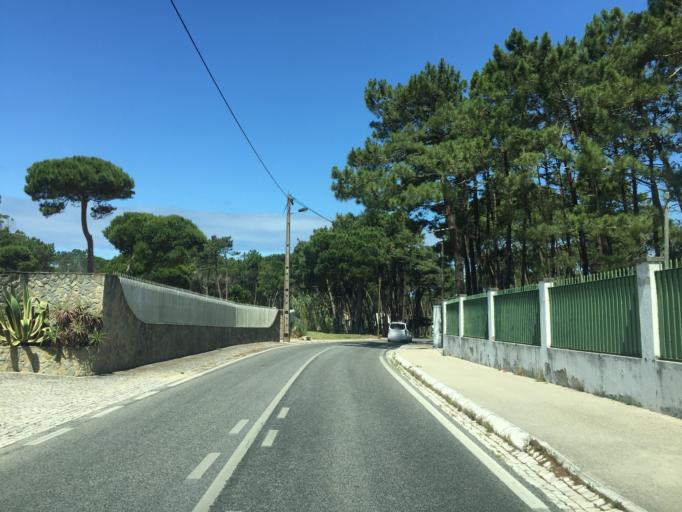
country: PT
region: Lisbon
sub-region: Sintra
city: Colares
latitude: 38.8327
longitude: -9.4524
